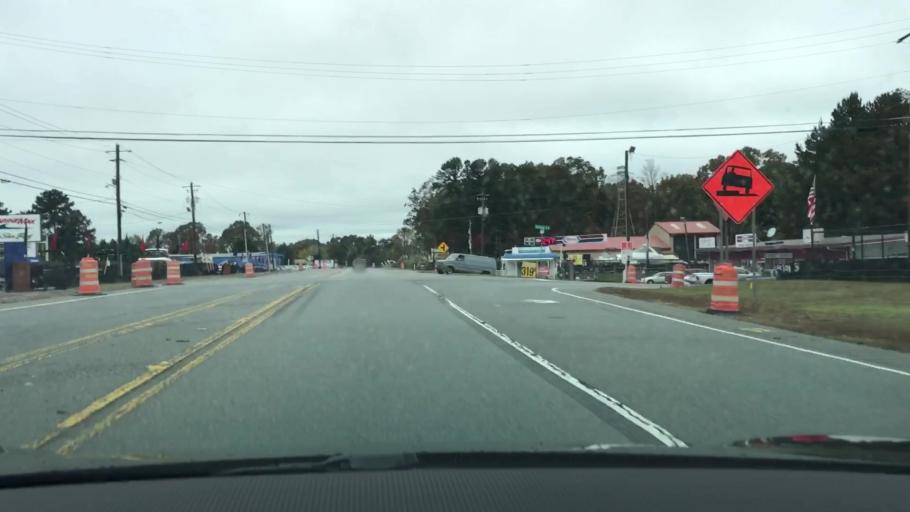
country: US
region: Georgia
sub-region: Gwinnett County
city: Buford
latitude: 34.1522
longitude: -83.9841
